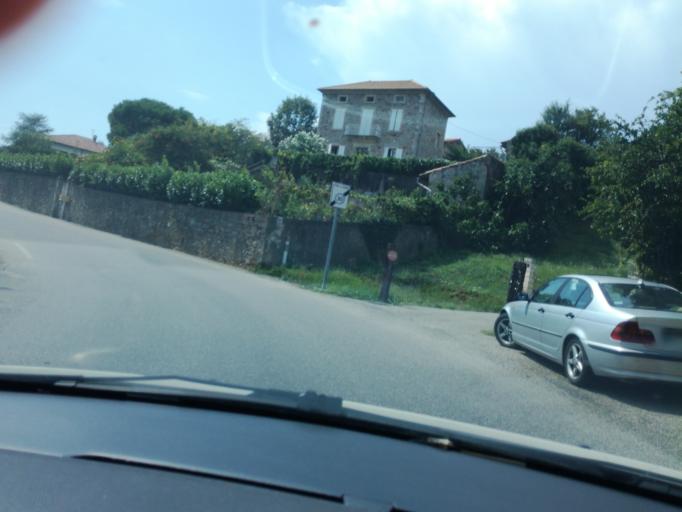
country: FR
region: Rhone-Alpes
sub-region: Departement de l'Ardeche
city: Labegude
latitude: 44.6384
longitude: 4.3696
